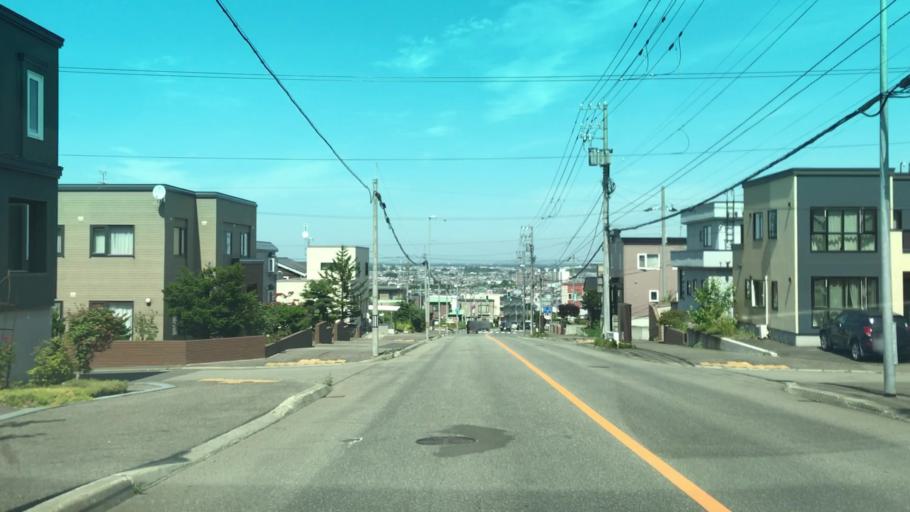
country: JP
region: Hokkaido
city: Sapporo
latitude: 43.1120
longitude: 141.2422
